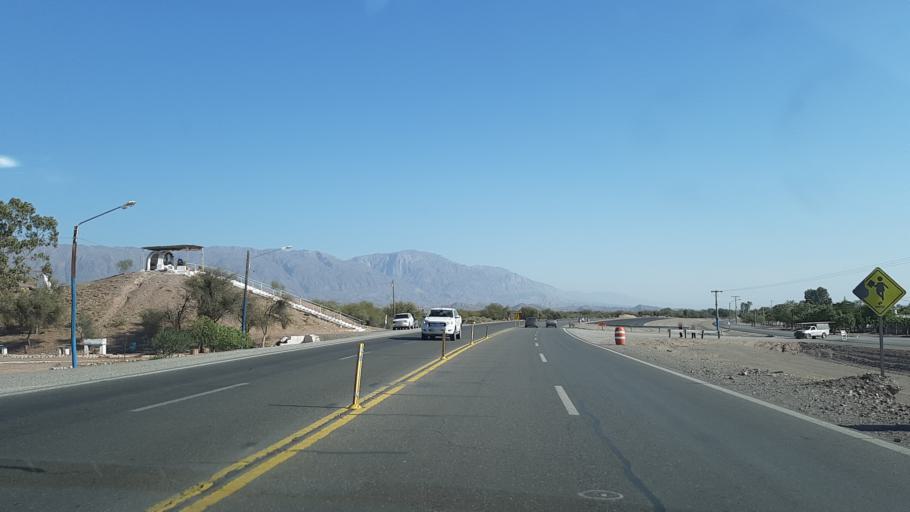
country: AR
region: San Juan
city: Villa Media Agua
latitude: -31.8605
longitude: -68.5367
